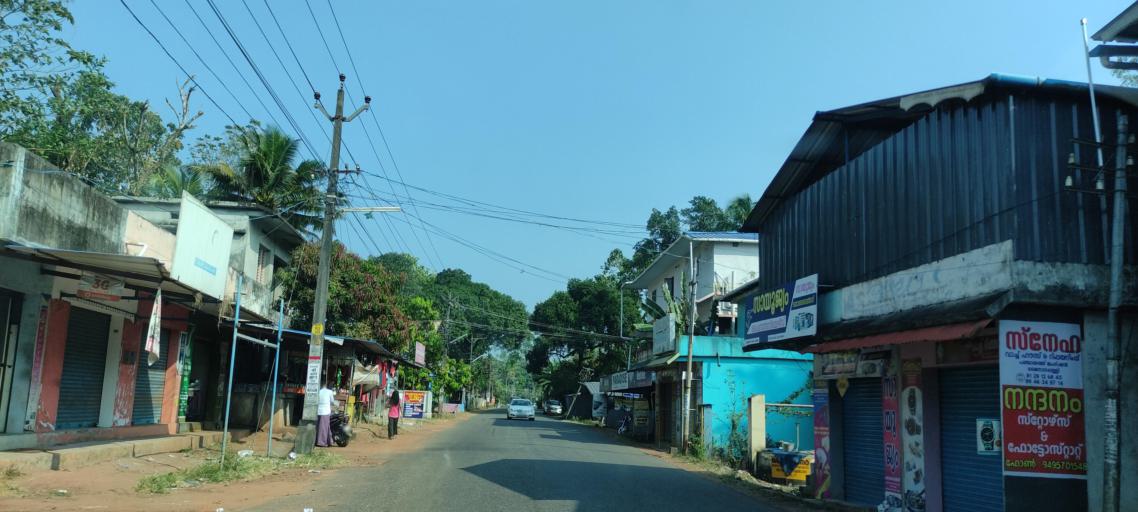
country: IN
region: Kerala
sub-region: Kollam
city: Panmana
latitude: 9.0419
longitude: 76.5897
